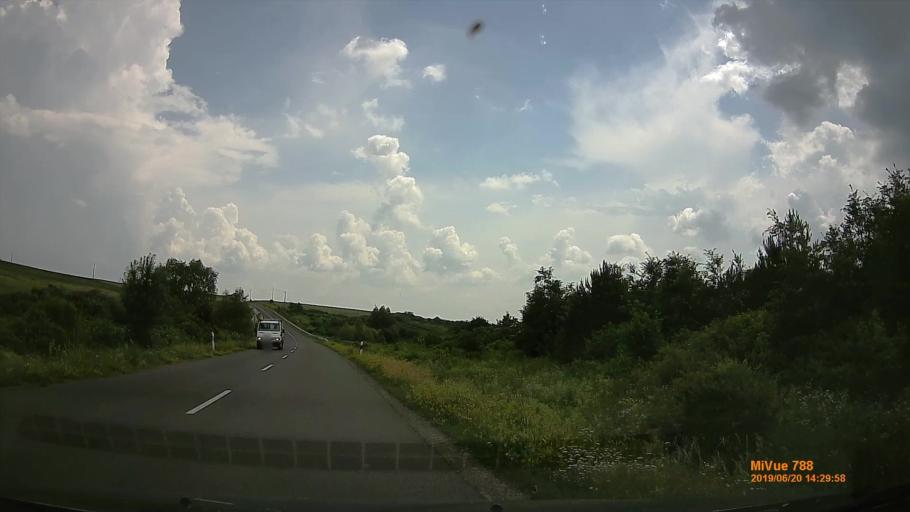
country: HU
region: Baranya
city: Hosszuheteny
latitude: 46.1539
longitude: 18.3433
